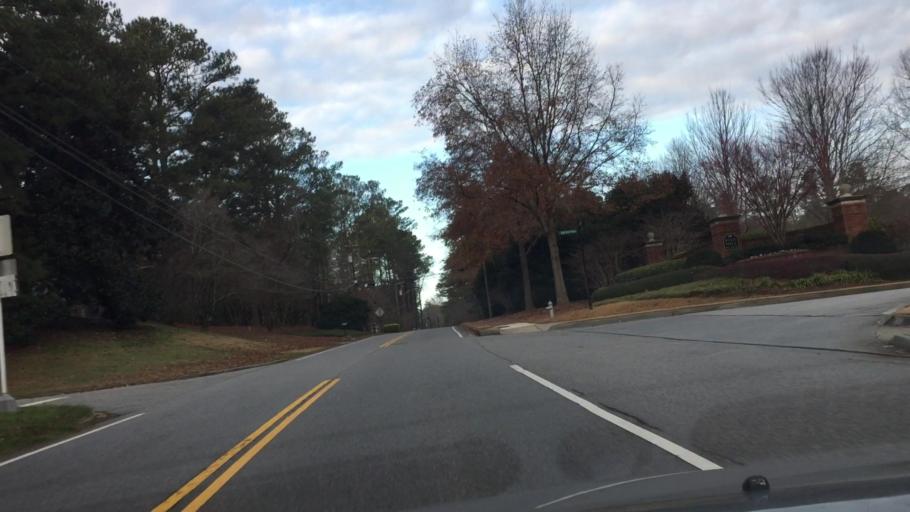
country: US
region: Georgia
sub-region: DeKalb County
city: Dunwoody
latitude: 33.9678
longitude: -84.3274
